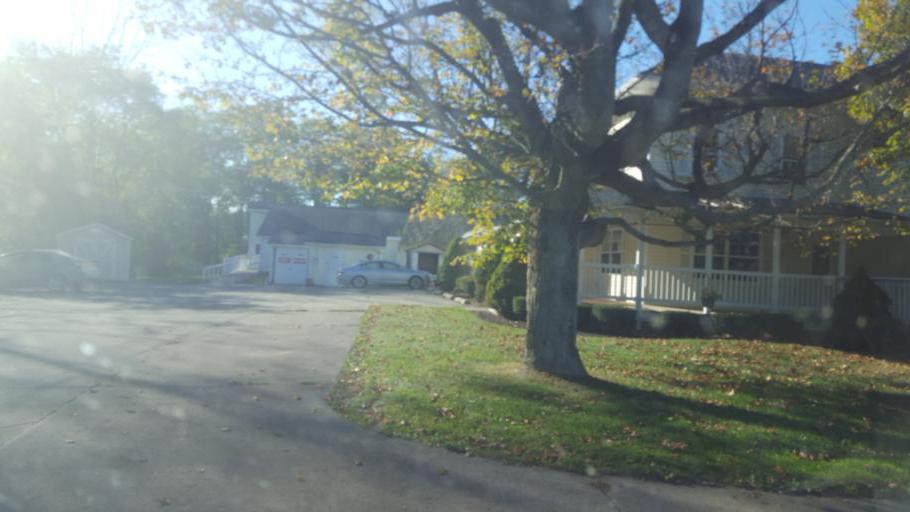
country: US
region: Ohio
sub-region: Richland County
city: Lexington
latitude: 40.6236
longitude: -82.6109
